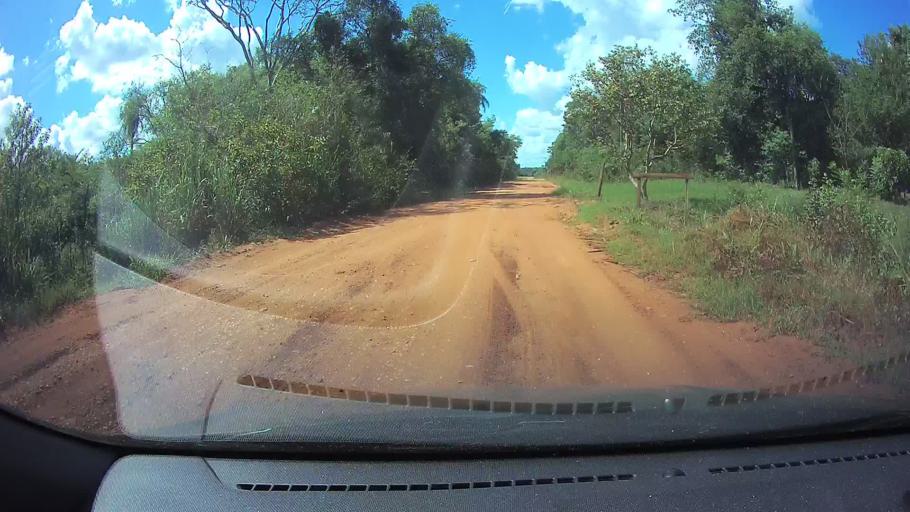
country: PY
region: Paraguari
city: La Colmena
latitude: -25.9014
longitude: -56.7930
